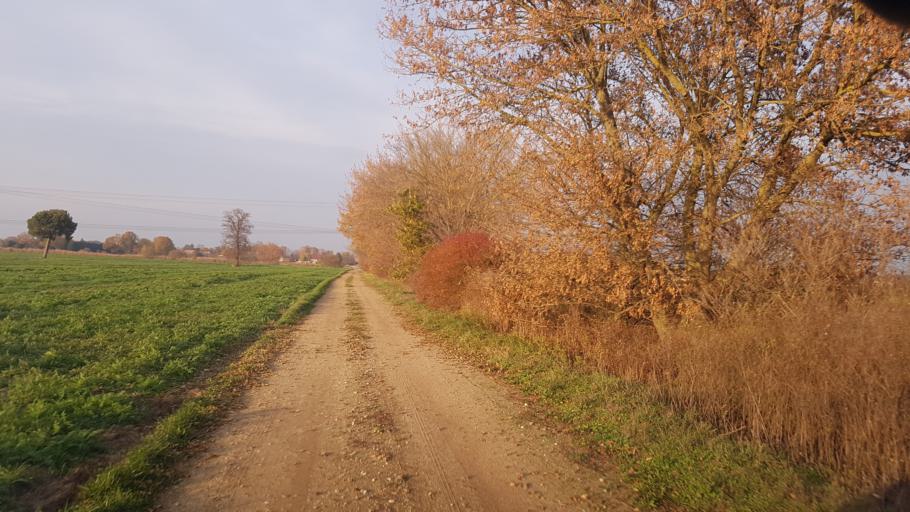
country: DE
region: Brandenburg
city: Schonewalde
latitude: 51.6508
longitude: 13.5991
